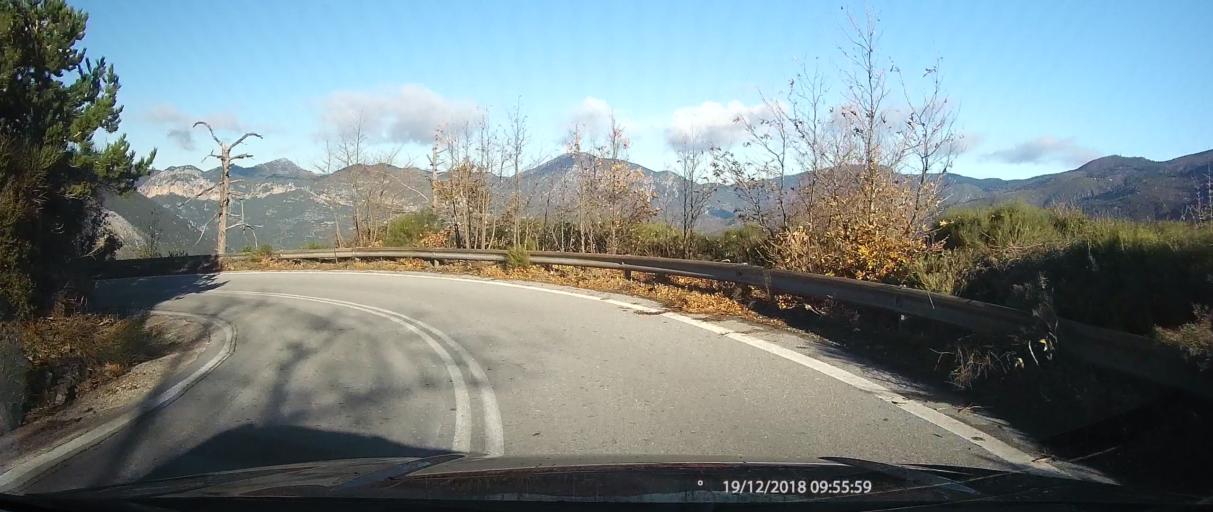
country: GR
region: Peloponnese
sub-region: Nomos Messinias
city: Paralia Vergas
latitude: 37.0843
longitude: 22.2432
